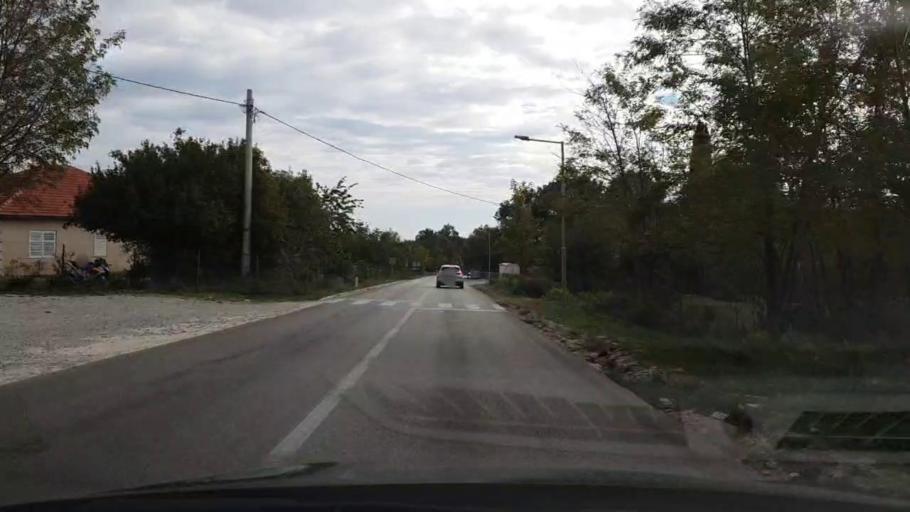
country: ME
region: Herceg Novi
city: Herceg-Novi
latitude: 42.4804
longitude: 18.5291
